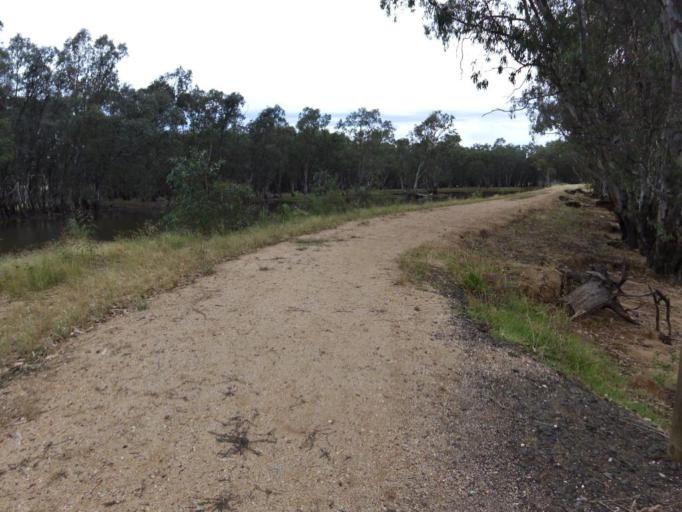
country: AU
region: Victoria
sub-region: Greater Bendigo
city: Kennington
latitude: -36.8685
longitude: 144.6243
